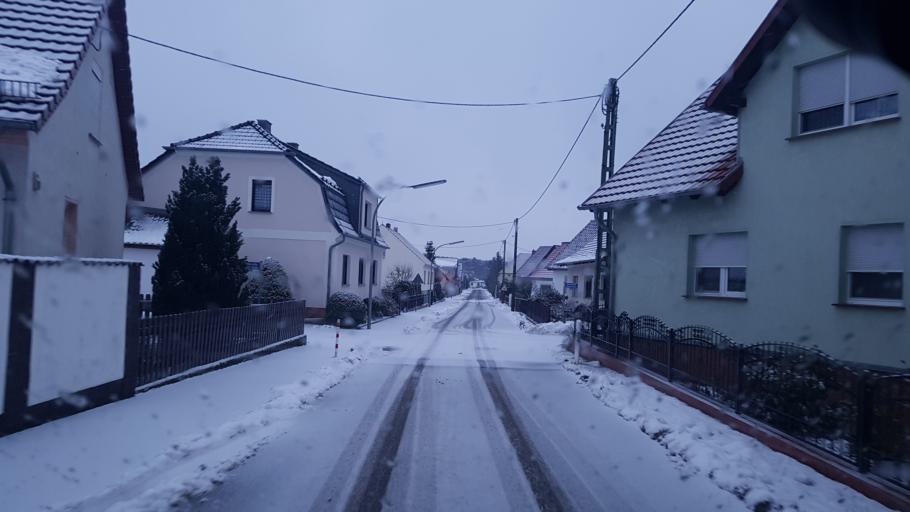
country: DE
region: Brandenburg
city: Janschwalde
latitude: 51.8966
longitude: 14.5087
